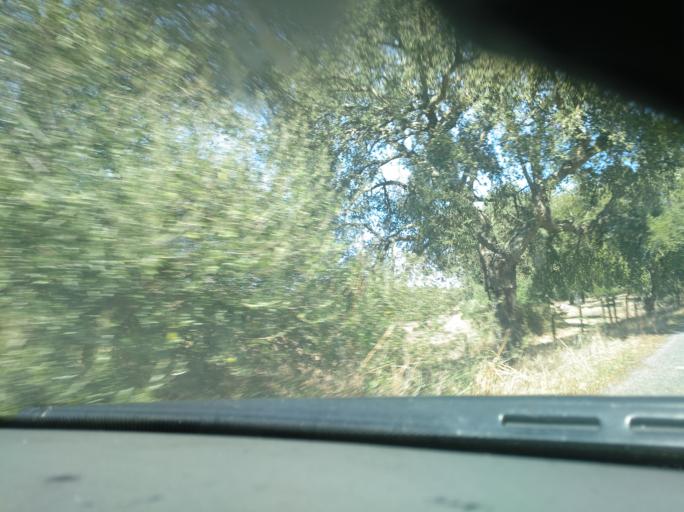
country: PT
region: Evora
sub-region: Arraiolos
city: Arraiolos
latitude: 38.6961
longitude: -8.0934
